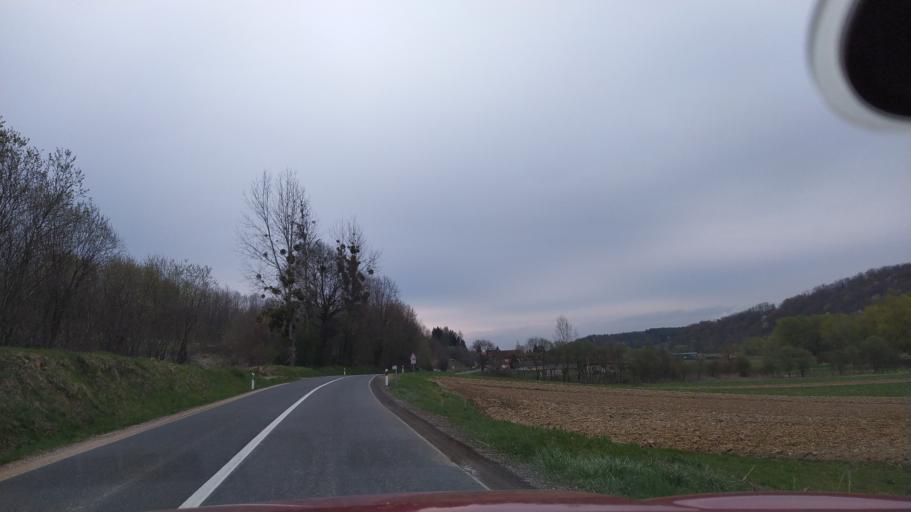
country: HR
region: Varazdinska
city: Jalzabet
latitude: 46.2205
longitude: 16.5377
